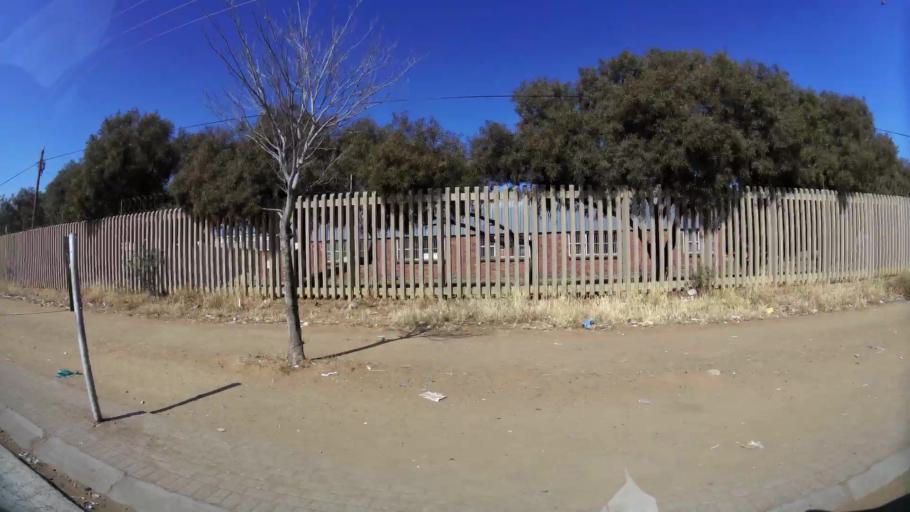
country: ZA
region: Orange Free State
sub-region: Mangaung Metropolitan Municipality
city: Bloemfontein
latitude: -29.1558
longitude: 26.2519
